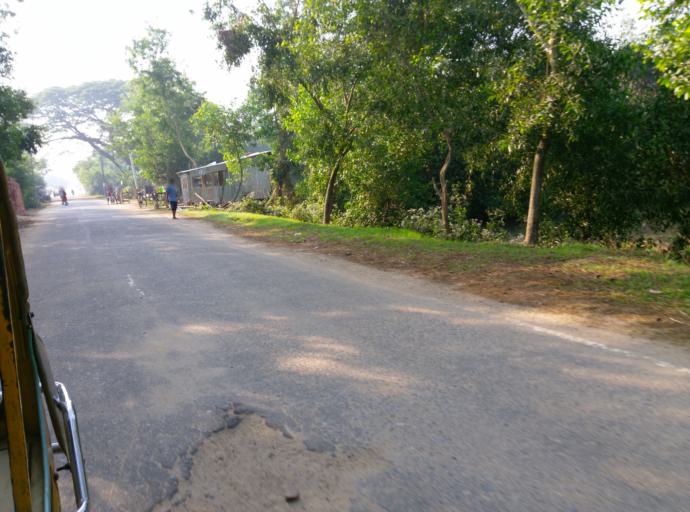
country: BD
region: Dhaka
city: Netrakona
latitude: 25.1315
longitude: 90.6630
